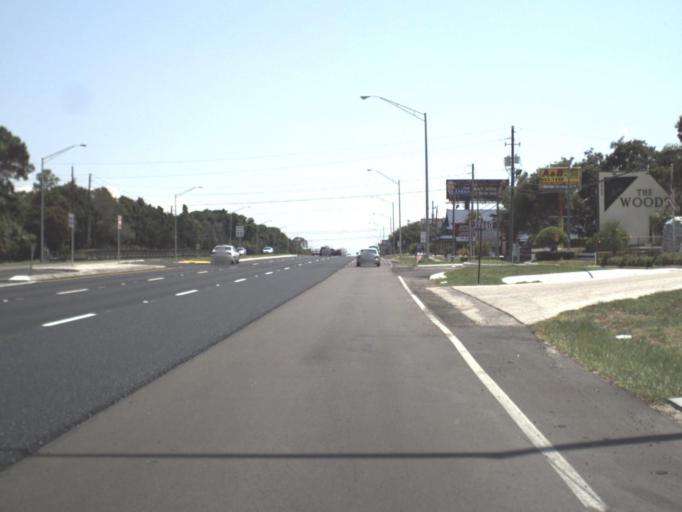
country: US
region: Florida
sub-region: Pinellas County
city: Tarpon Springs
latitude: 28.1329
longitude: -82.7404
